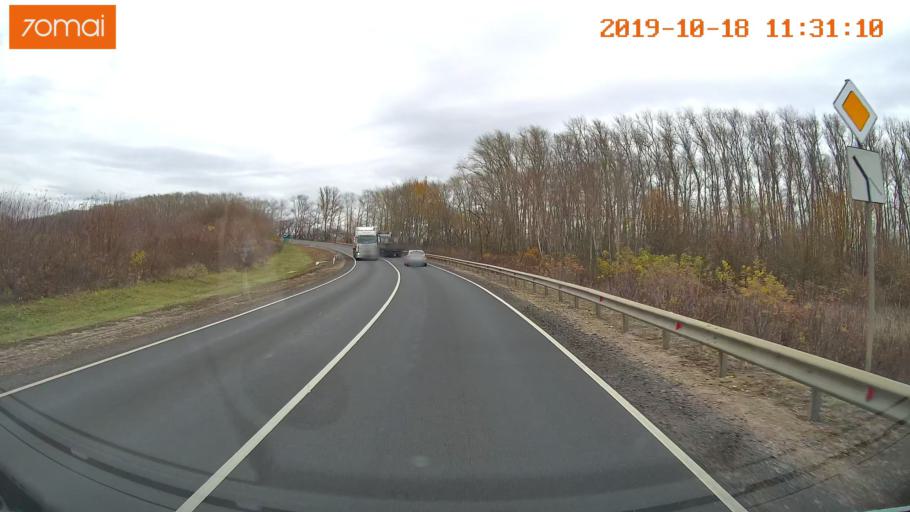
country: RU
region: Rjazan
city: Oktyabr'skiy
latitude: 54.1420
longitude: 38.6914
